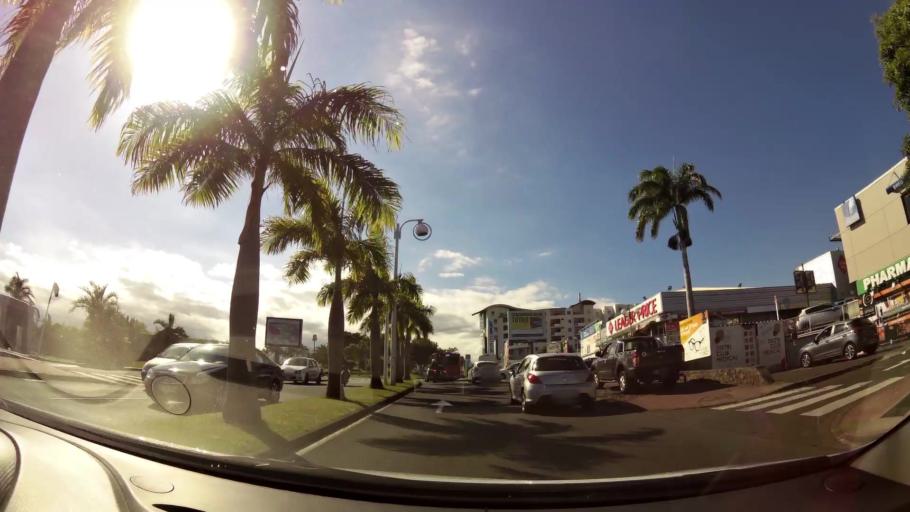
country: RE
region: Reunion
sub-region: Reunion
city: Saint-Pierre
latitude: -21.3309
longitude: 55.4723
